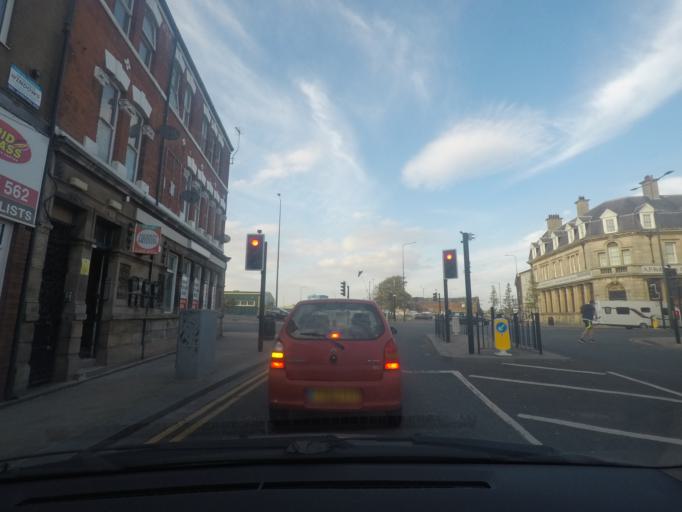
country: GB
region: England
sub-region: North East Lincolnshire
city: Grimsby
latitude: 53.5748
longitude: -0.0729
